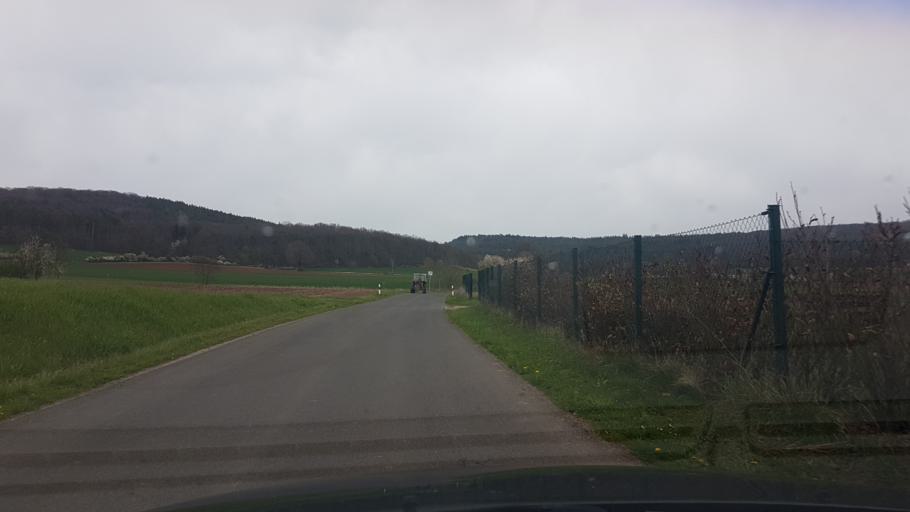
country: DE
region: Bavaria
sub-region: Upper Franconia
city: Reckendorf
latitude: 50.0386
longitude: 10.8369
